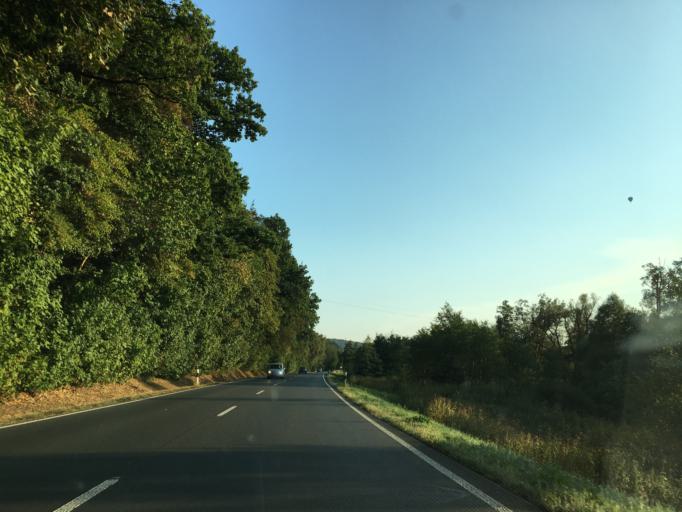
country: DE
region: Hesse
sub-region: Regierungsbezirk Giessen
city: Colbe
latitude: 50.8656
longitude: 8.7922
